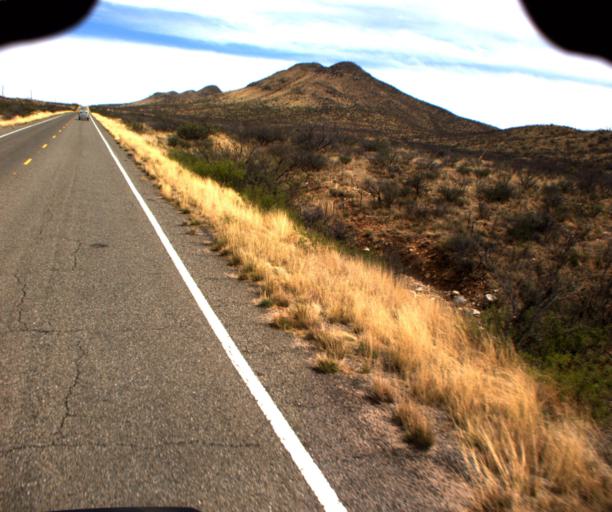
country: US
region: Arizona
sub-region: Cochise County
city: Willcox
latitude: 32.1830
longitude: -109.6436
